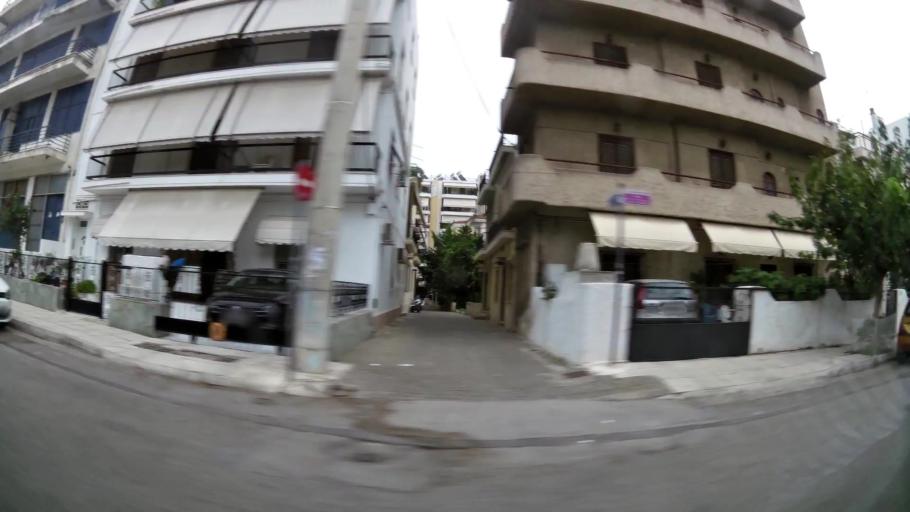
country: GR
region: Attica
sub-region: Nomos Piraios
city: Agios Ioannis Rentis
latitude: 37.9599
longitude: 23.6692
